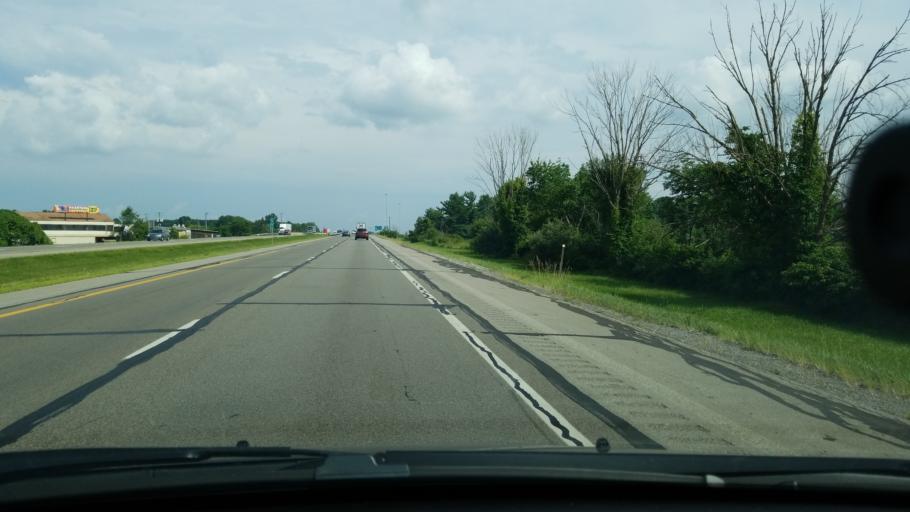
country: US
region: Ohio
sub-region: Mahoning County
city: Boardman
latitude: 40.9725
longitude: -80.6646
